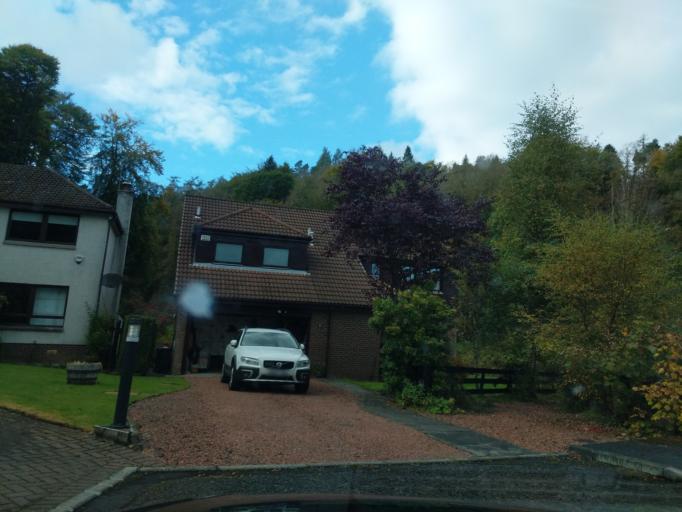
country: GB
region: Scotland
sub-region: The Scottish Borders
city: West Linton
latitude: 55.7543
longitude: -3.3617
